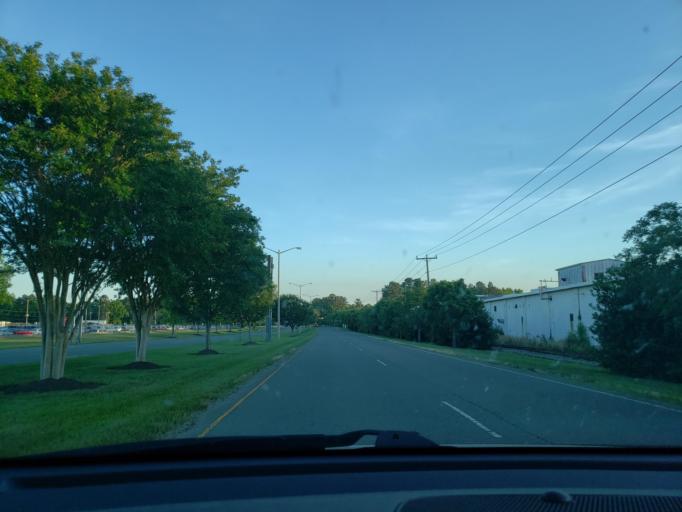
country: US
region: Virginia
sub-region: Henrico County
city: Fort Lee
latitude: 37.5020
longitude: -77.3393
